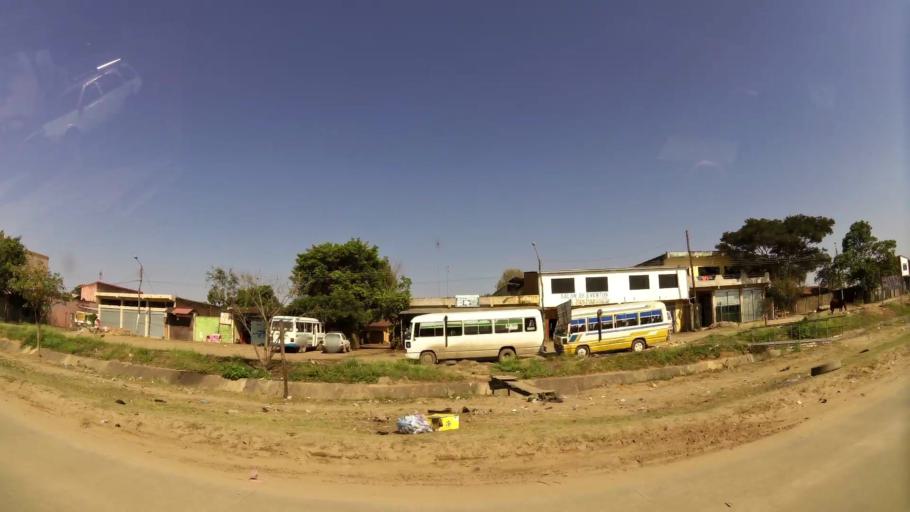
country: BO
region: Santa Cruz
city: Cotoca
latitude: -17.8156
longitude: -63.1133
